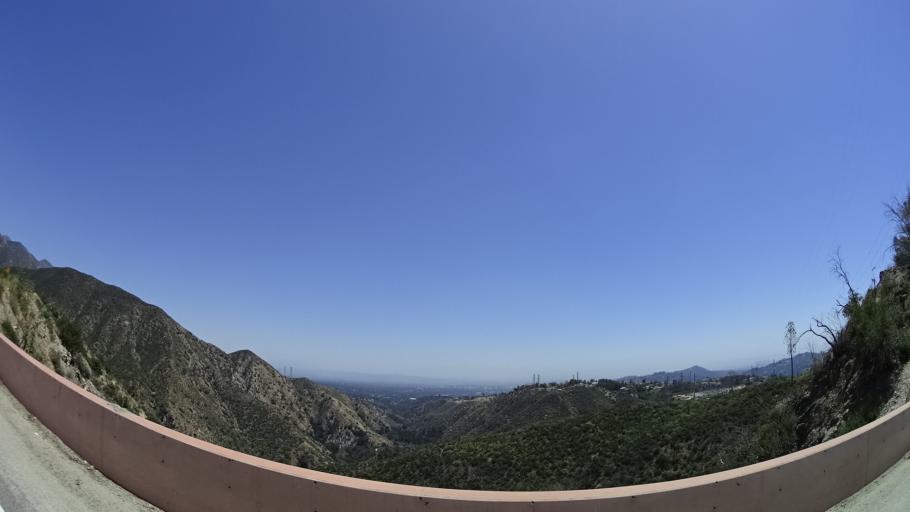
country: US
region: California
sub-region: Los Angeles County
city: La Canada Flintridge
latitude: 34.2288
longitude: -118.1851
